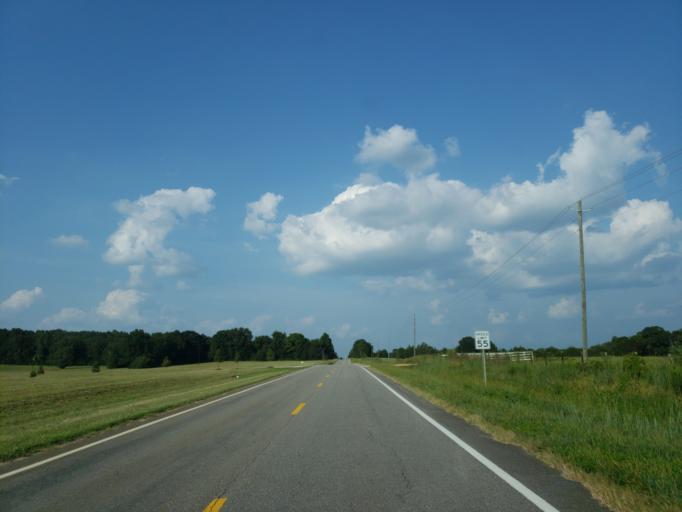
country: US
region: Alabama
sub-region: Greene County
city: Eutaw
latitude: 32.7627
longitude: -88.0067
